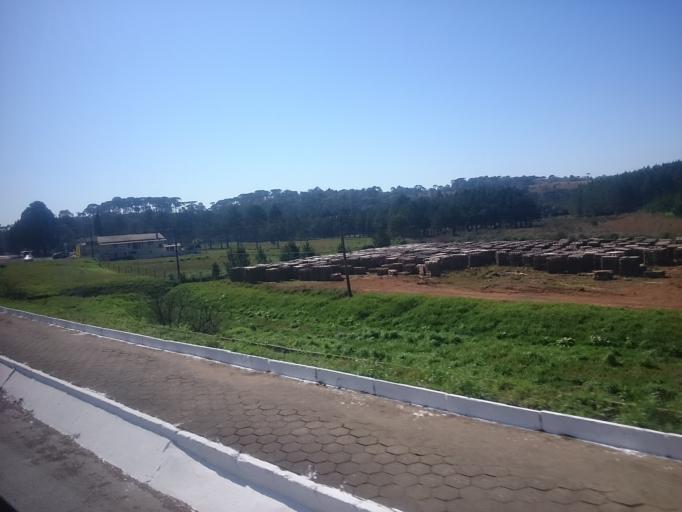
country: BR
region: Santa Catarina
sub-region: Curitibanos
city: Curitibanos
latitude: -27.1613
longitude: -50.4668
